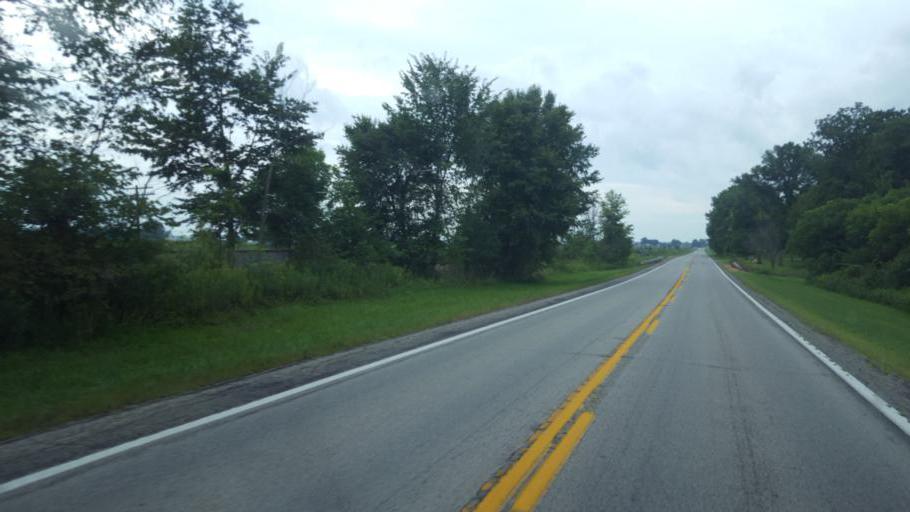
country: US
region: Ohio
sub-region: Delaware County
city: Delaware
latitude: 40.3382
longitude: -83.0016
